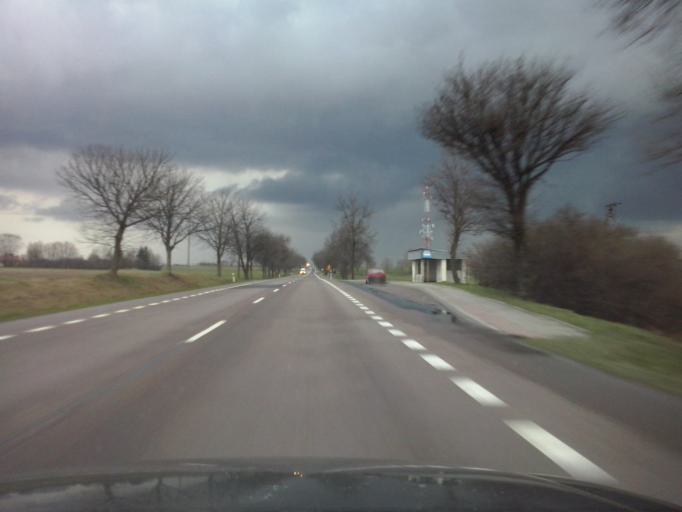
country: PL
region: Lublin Voivodeship
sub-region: Powiat chelmski
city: Rejowiec Fabryczny
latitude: 51.1771
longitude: 23.2287
